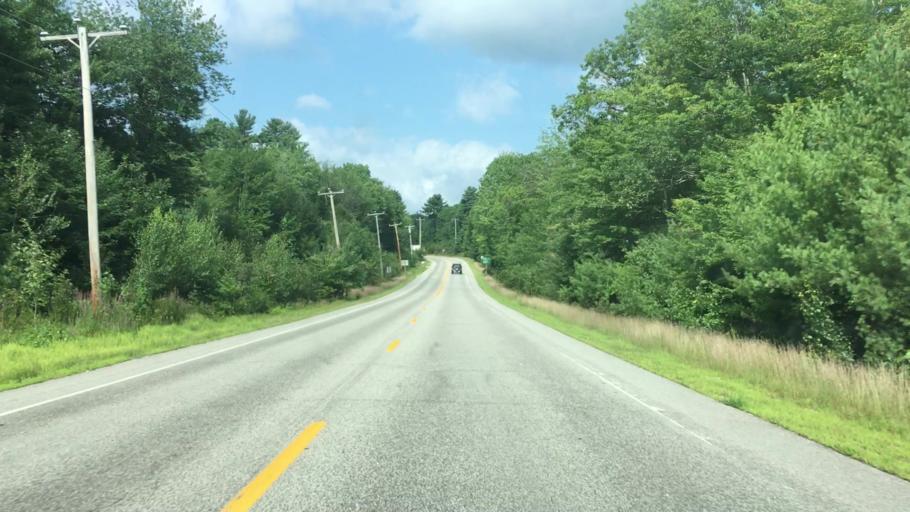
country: US
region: Maine
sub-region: Androscoggin County
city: Minot
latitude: 44.0277
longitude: -70.3225
